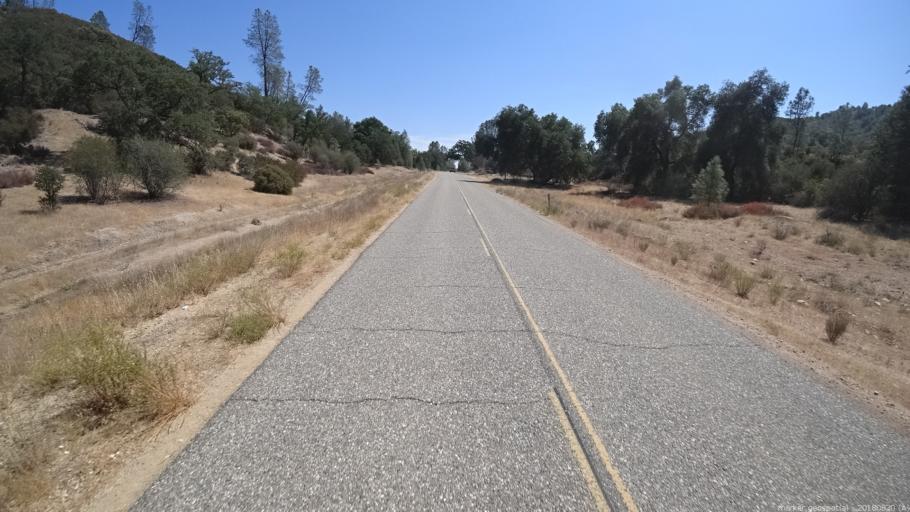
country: US
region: California
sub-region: Monterey County
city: King City
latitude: 36.0232
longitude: -121.2871
